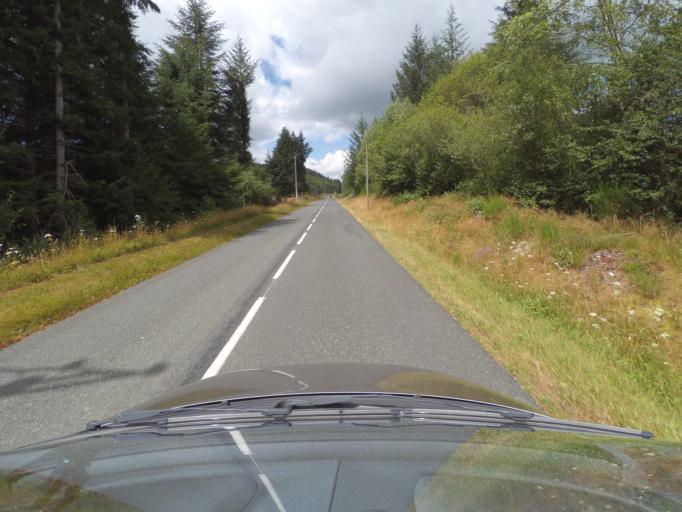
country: FR
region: Limousin
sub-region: Departement de la Haute-Vienne
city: Peyrat-le-Chateau
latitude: 45.8885
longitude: 1.8874
